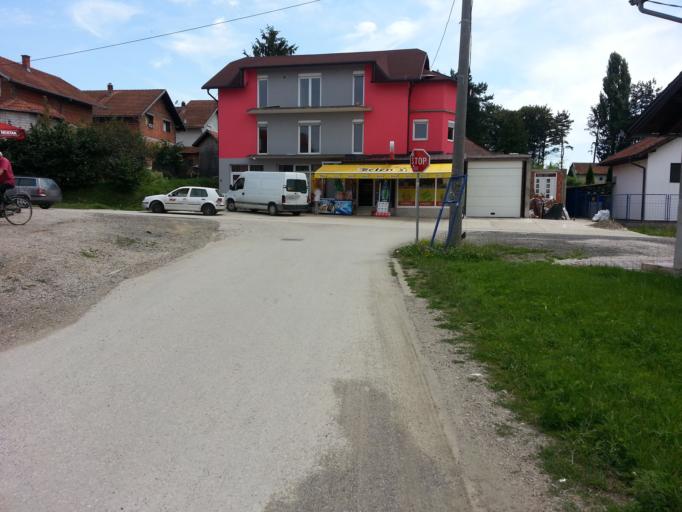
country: BA
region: Republika Srpska
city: Prijedor
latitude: 44.9869
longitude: 16.7297
